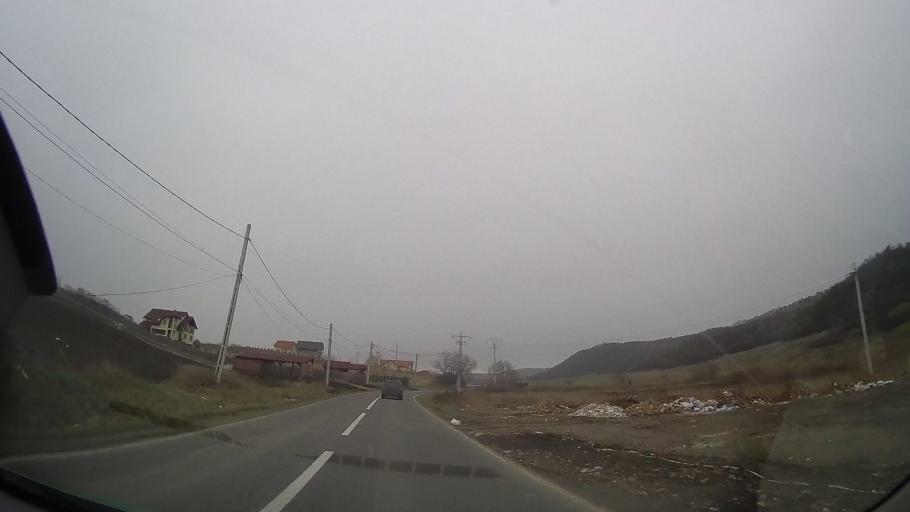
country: RO
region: Mures
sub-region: Comuna Ceausu de Campie
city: Ceausu de Campie
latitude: 46.6239
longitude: 24.5222
